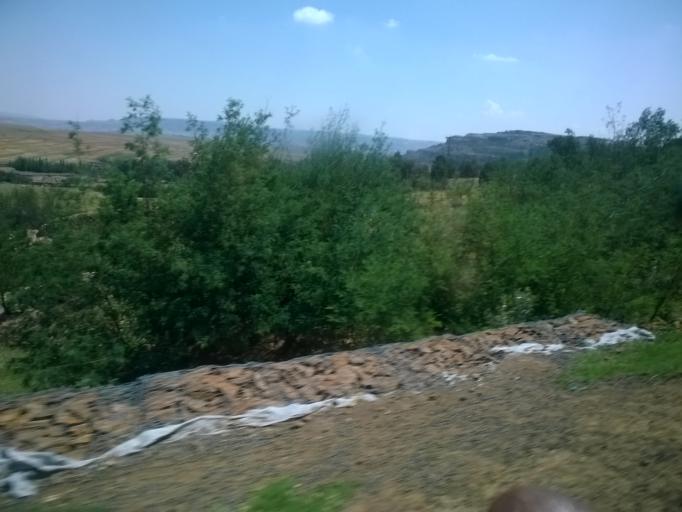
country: LS
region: Berea
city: Teyateyaneng
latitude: -29.1174
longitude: 27.8173
